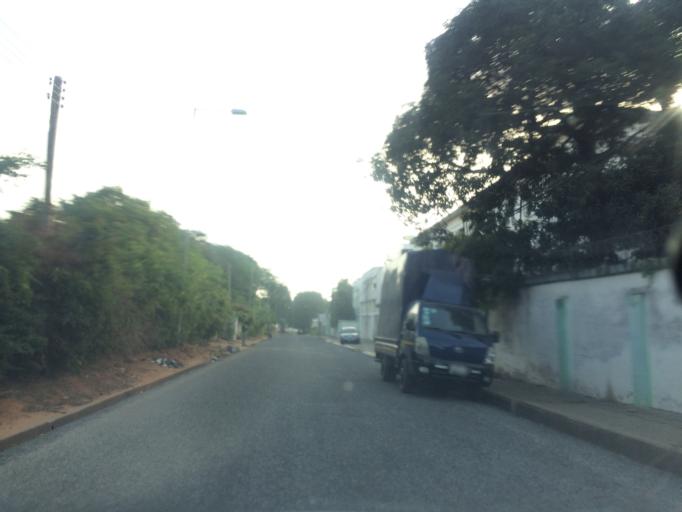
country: GH
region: Greater Accra
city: Accra
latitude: 5.5619
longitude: -0.2019
